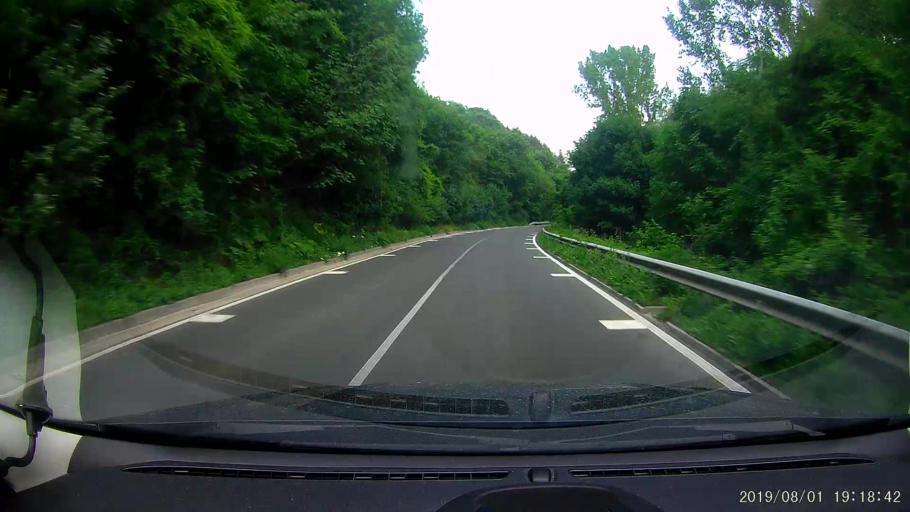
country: BG
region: Shumen
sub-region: Obshtina Smyadovo
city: Smyadovo
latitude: 42.9094
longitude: 26.9401
